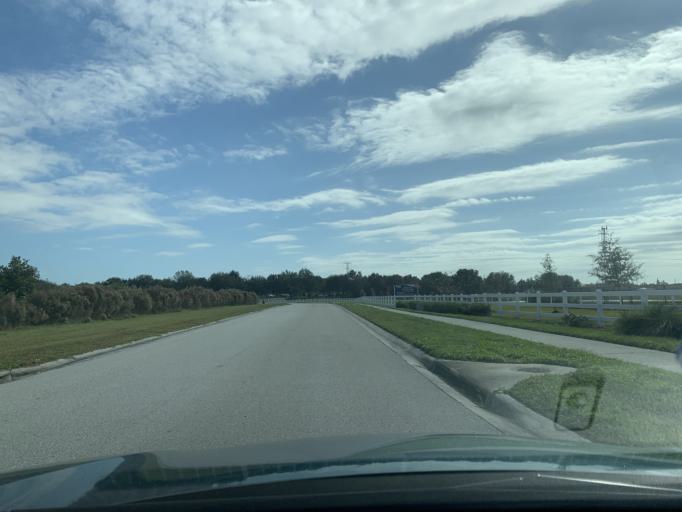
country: US
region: Florida
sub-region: Pasco County
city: Trinity
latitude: 28.1905
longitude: -82.6714
